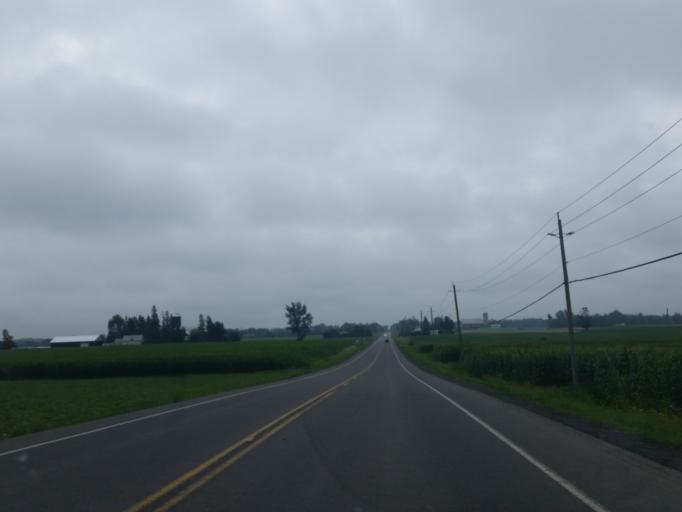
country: CA
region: Ontario
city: Clarence-Rockland
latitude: 45.4360
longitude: -75.4350
